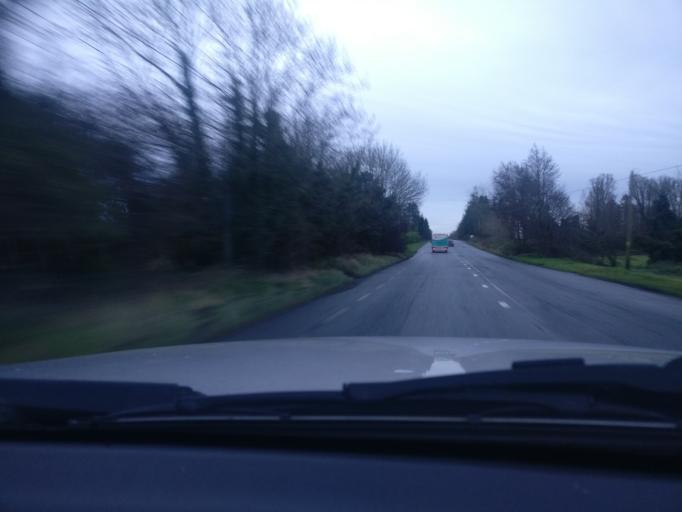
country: IE
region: Leinster
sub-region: An Mhi
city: Kells
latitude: 53.7050
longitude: -6.7965
